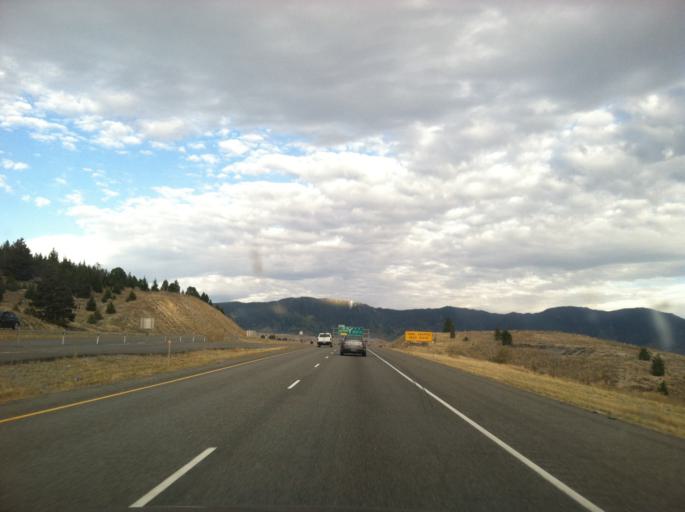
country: US
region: Montana
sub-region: Silver Bow County
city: Butte
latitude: 46.0054
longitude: -112.5826
